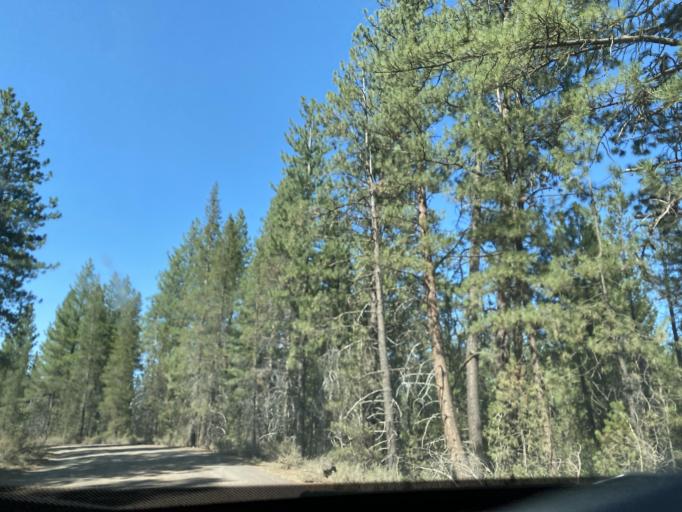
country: US
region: Oregon
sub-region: Deschutes County
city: Sunriver
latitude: 43.8764
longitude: -121.4667
